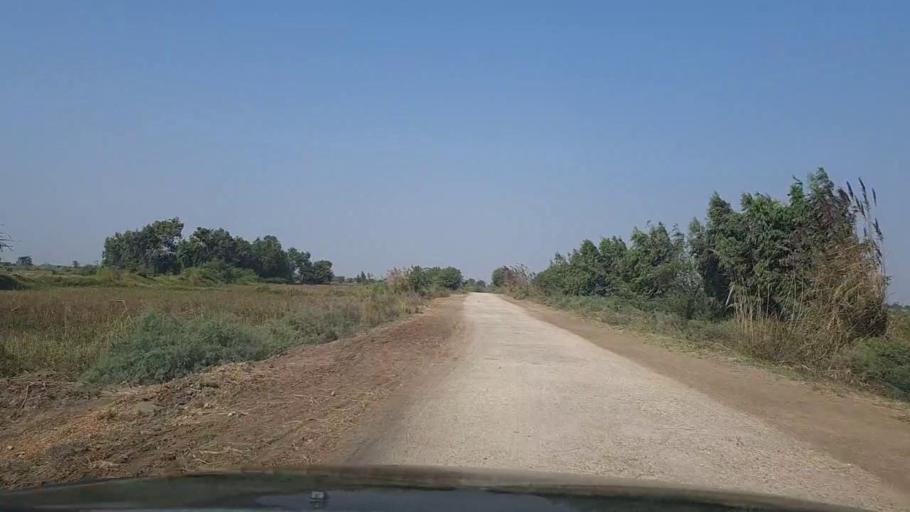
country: PK
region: Sindh
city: Thatta
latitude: 24.6185
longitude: 67.8167
